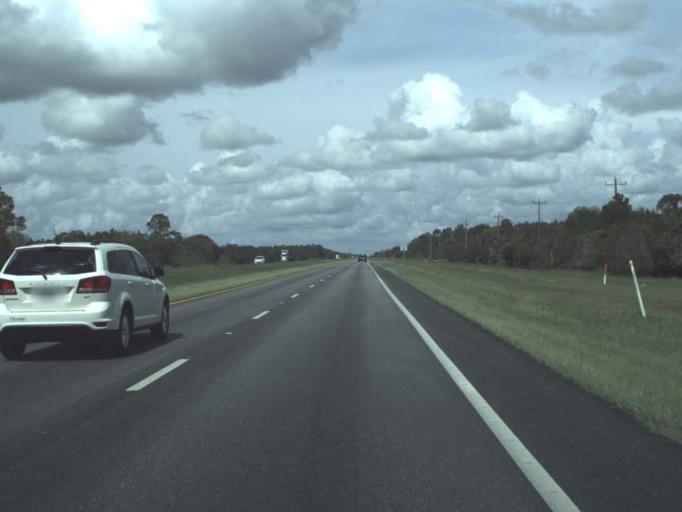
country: US
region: Florida
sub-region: Lee County
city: Suncoast Estates
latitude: 26.7858
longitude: -81.9413
